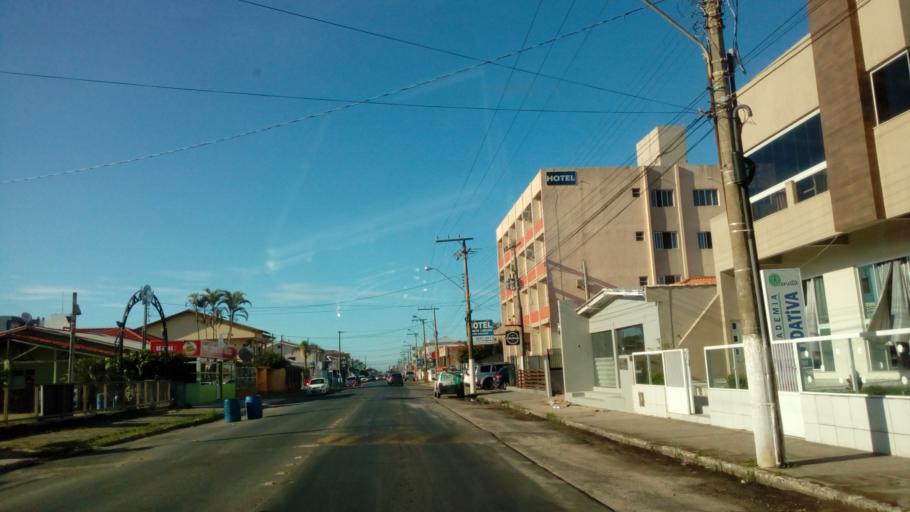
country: BR
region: Santa Catarina
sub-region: Laguna
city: Laguna
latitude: -28.4890
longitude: -48.7708
